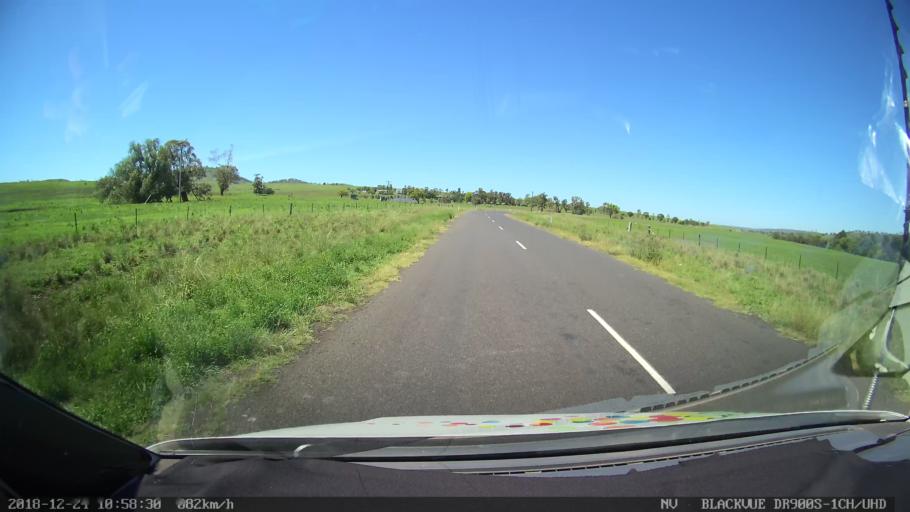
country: AU
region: New South Wales
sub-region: Upper Hunter Shire
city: Merriwa
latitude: -32.0482
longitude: 150.4061
